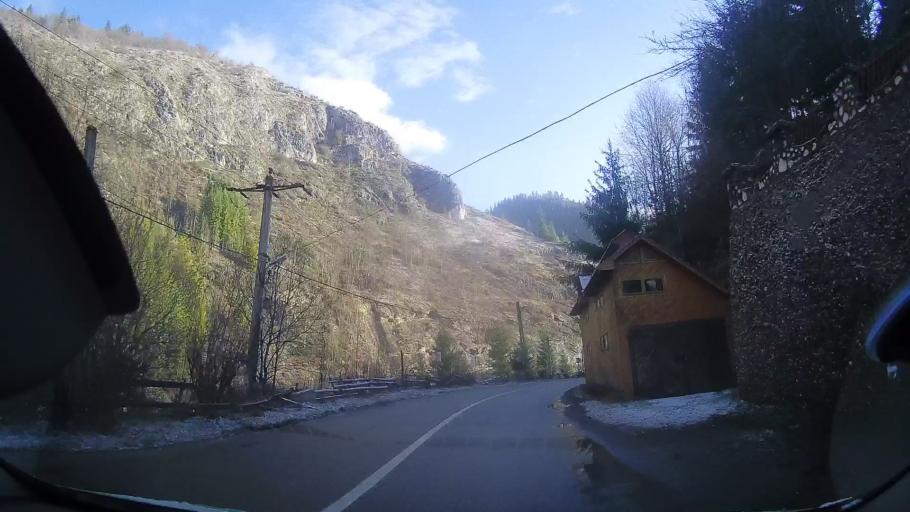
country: RO
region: Alba
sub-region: Comuna Scarisoara
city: Scarisoara
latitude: 46.4629
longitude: 22.8850
